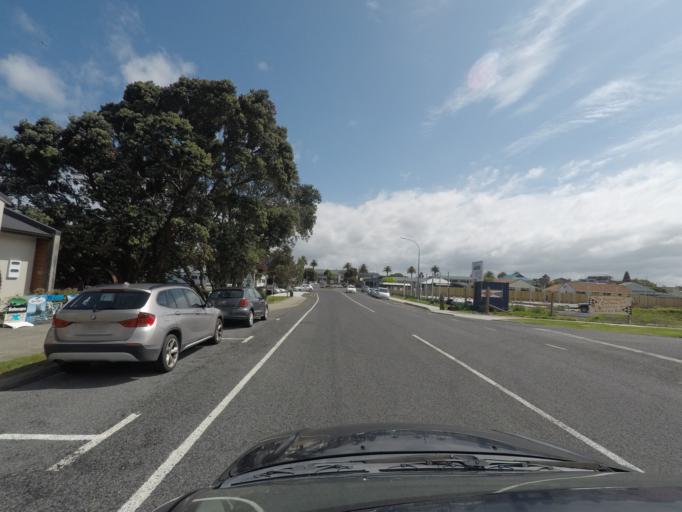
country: NZ
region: Waikato
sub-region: Waikato District
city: Raglan
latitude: -37.8020
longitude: 174.8686
